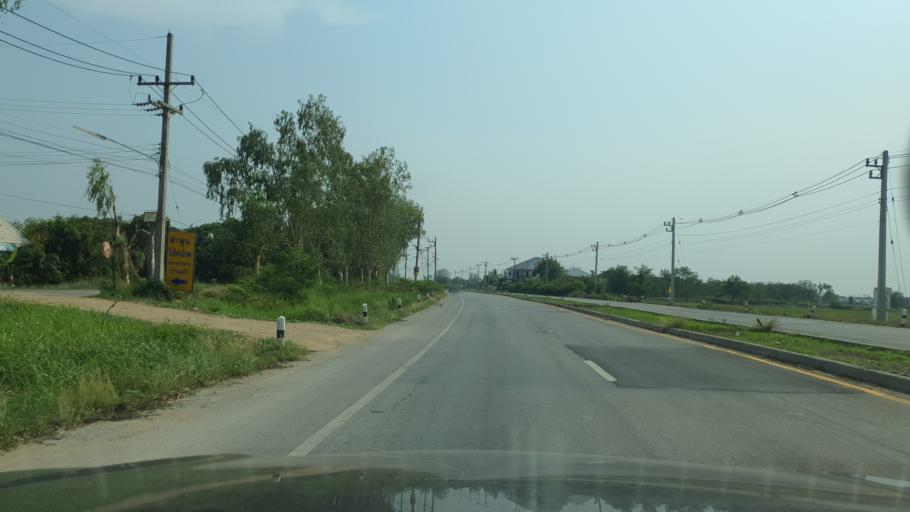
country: TH
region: Lamphun
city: Lamphun
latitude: 18.5921
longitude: 98.9986
